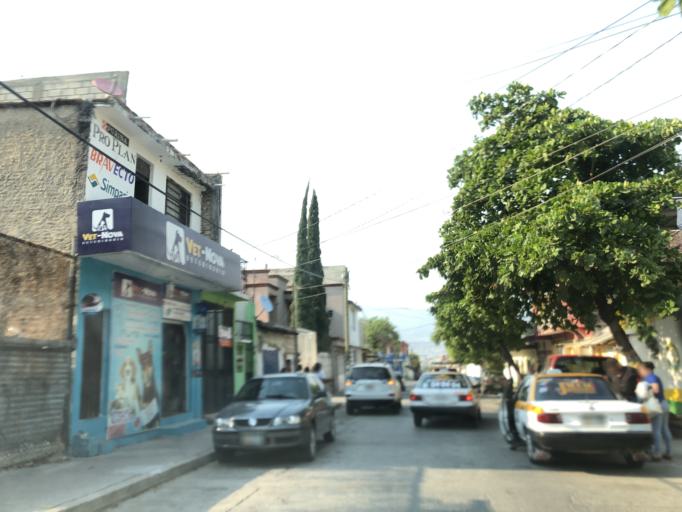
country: MX
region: Chiapas
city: Tuxtla Gutierrez
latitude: 16.7462
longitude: -93.1226
